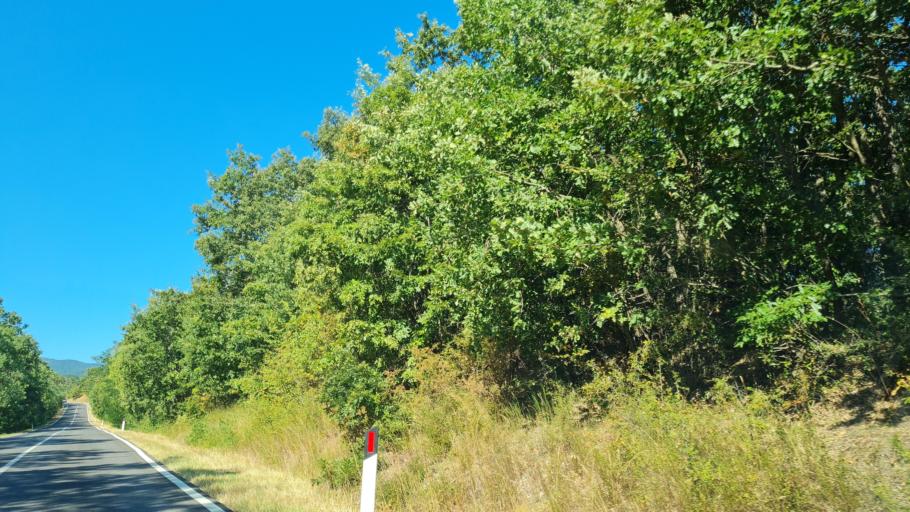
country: IT
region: Tuscany
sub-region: Provincia di Siena
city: Abbadia San Salvatore
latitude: 42.9157
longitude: 11.6931
